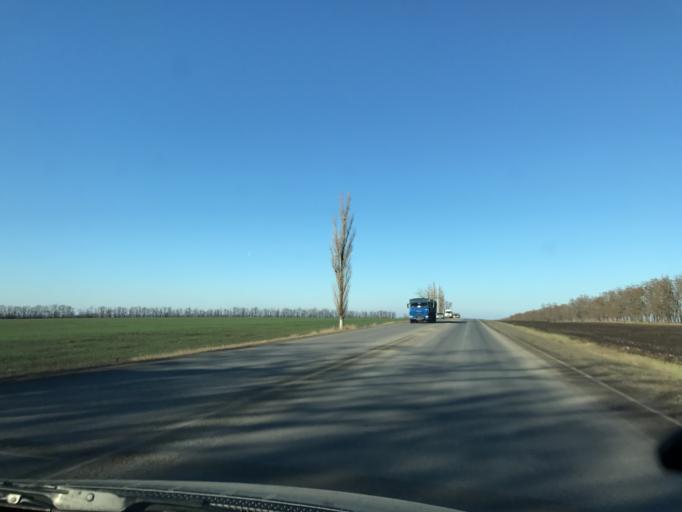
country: RU
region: Rostov
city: Kagal'nitskaya
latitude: 46.8441
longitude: 40.2157
